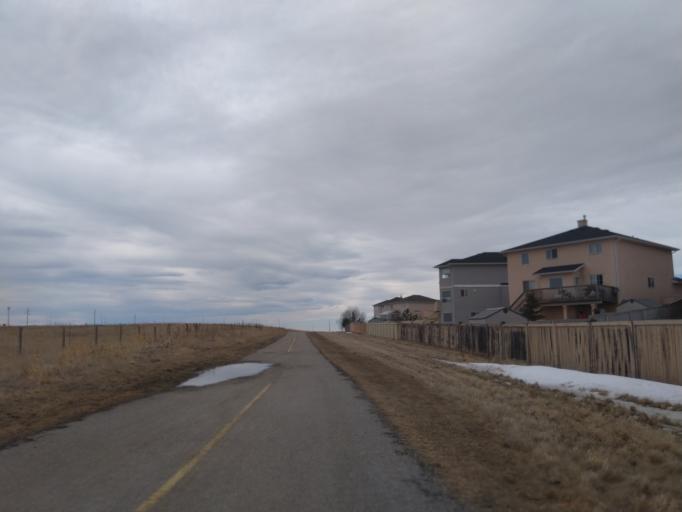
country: CA
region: Alberta
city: Chestermere
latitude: 51.1028
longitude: -113.9228
